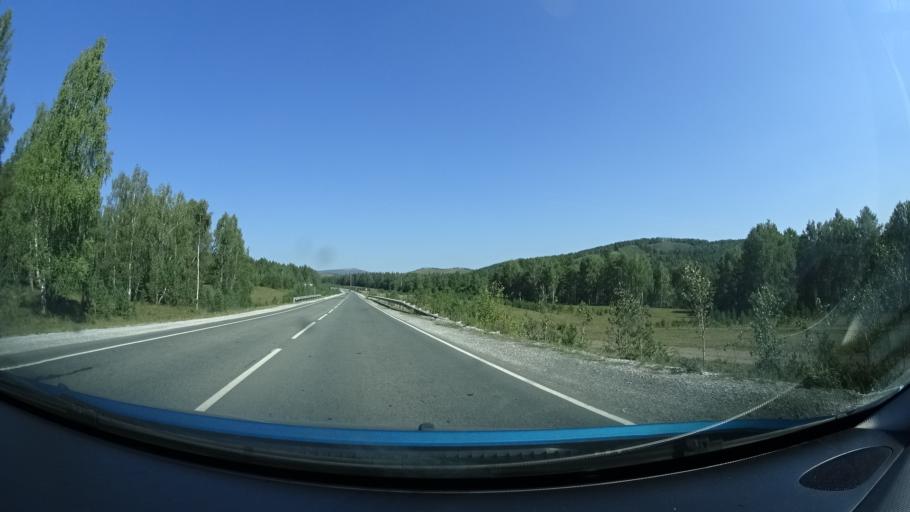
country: RU
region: Bashkortostan
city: Abzakovo
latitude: 53.8461
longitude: 58.5826
